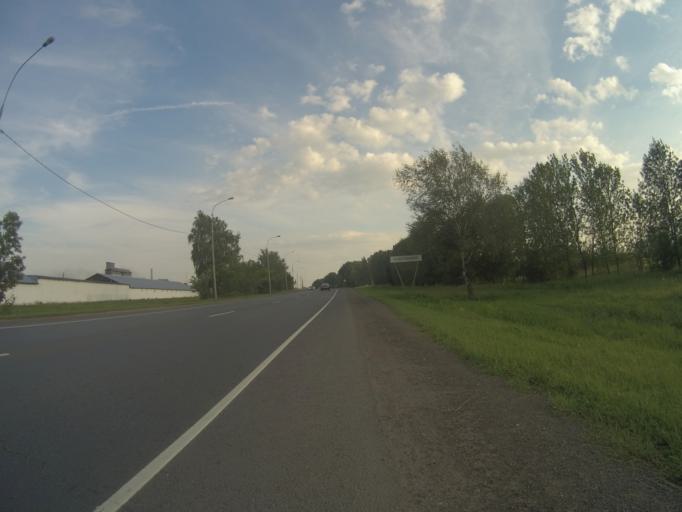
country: RU
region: Vladimir
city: Suzdal'
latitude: 56.3294
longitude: 40.4723
